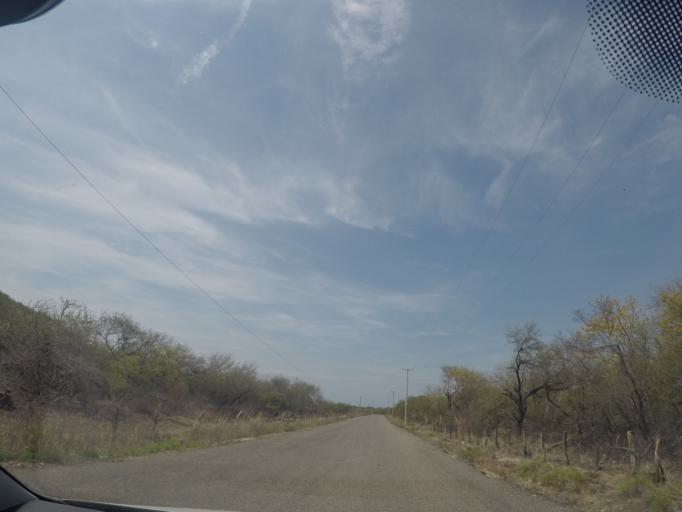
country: MX
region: Oaxaca
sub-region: Salina Cruz
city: Salina Cruz
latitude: 16.2071
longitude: -95.1217
